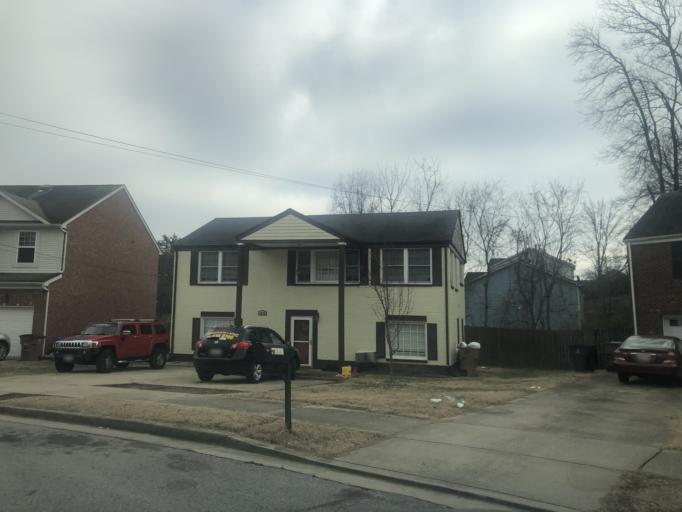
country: US
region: Tennessee
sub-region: Rutherford County
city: La Vergne
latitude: 36.0796
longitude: -86.6425
